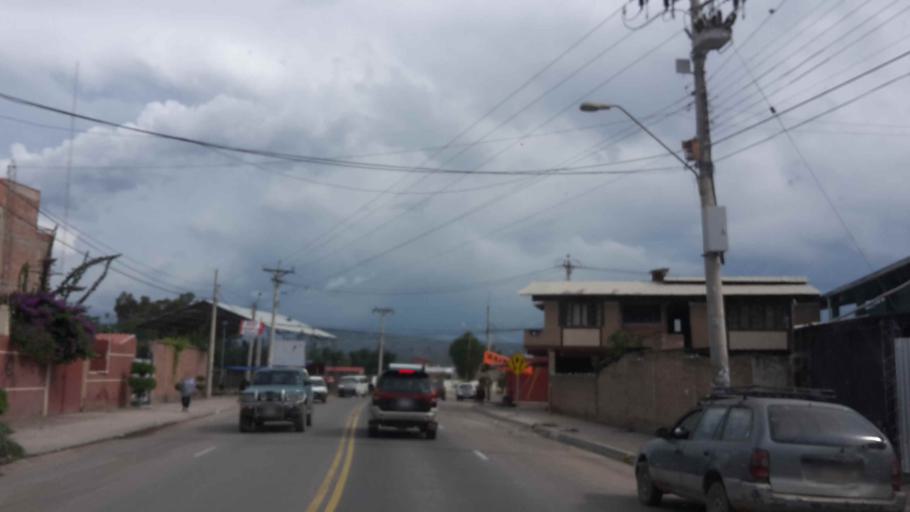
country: BO
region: Cochabamba
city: Cochabamba
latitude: -17.3823
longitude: -66.2513
